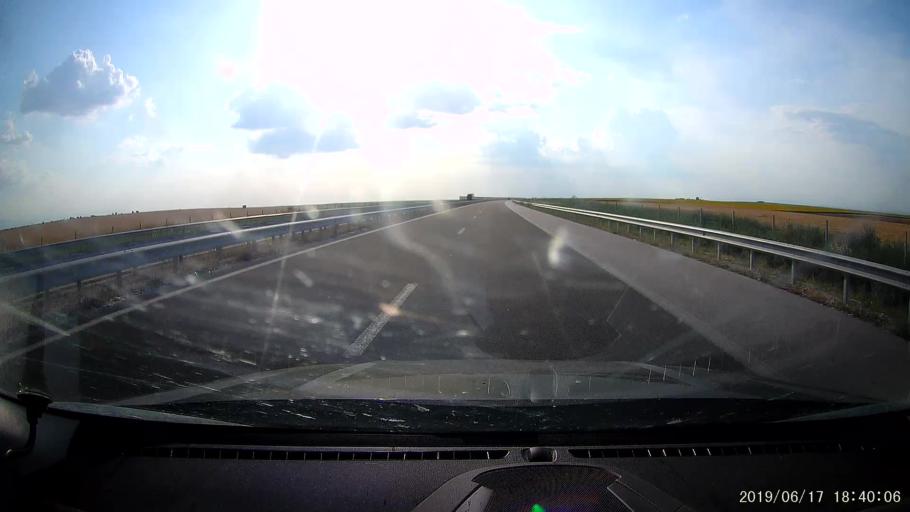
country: BG
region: Stara Zagora
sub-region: Obshtina Chirpan
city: Chirpan
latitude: 42.1515
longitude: 25.2878
